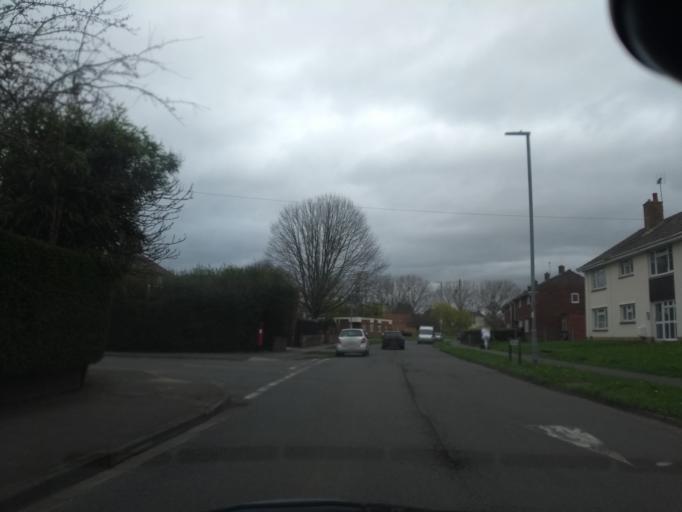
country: GB
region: England
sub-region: Somerset
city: Taunton
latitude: 51.0292
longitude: -3.0946
